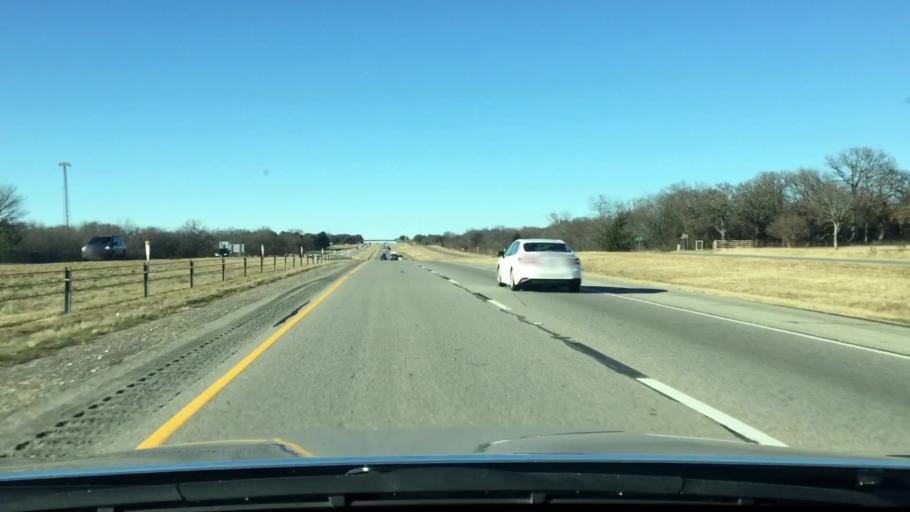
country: US
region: Texas
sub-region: Johnson County
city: Alvarado
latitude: 32.3684
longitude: -97.2015
